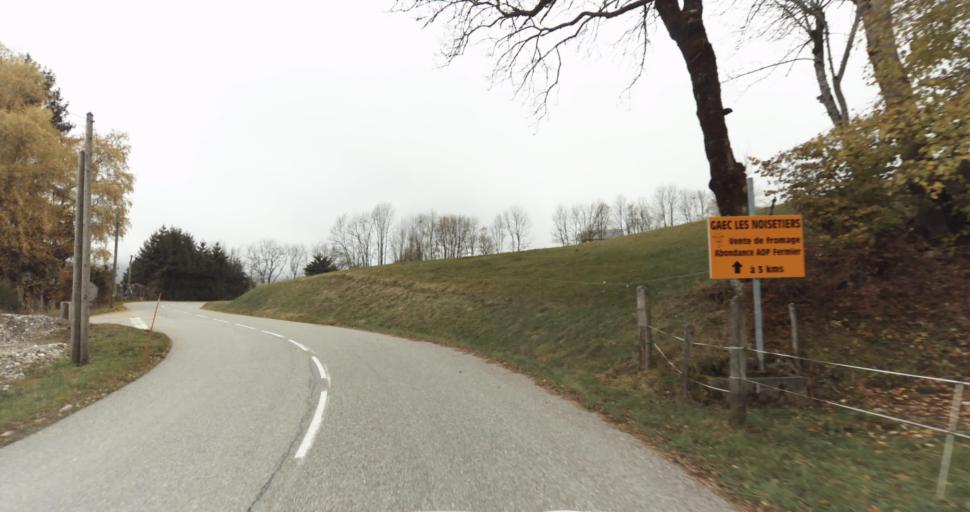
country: FR
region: Rhone-Alpes
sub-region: Departement de la Haute-Savoie
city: Saint-Jorioz
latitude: 45.7912
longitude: 6.1352
